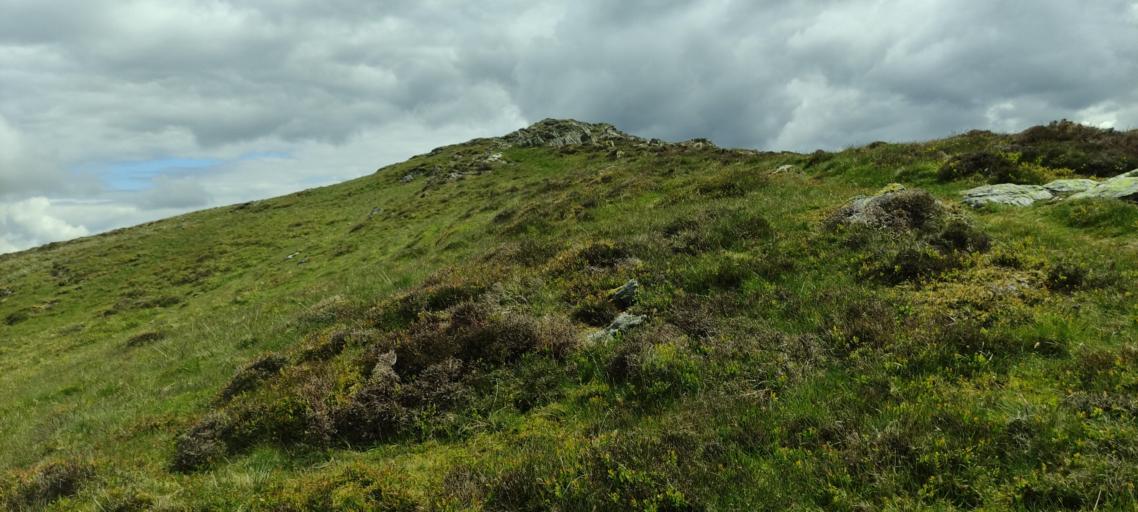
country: GB
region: England
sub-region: Cumbria
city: Cockermouth
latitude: 54.5687
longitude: -3.3717
